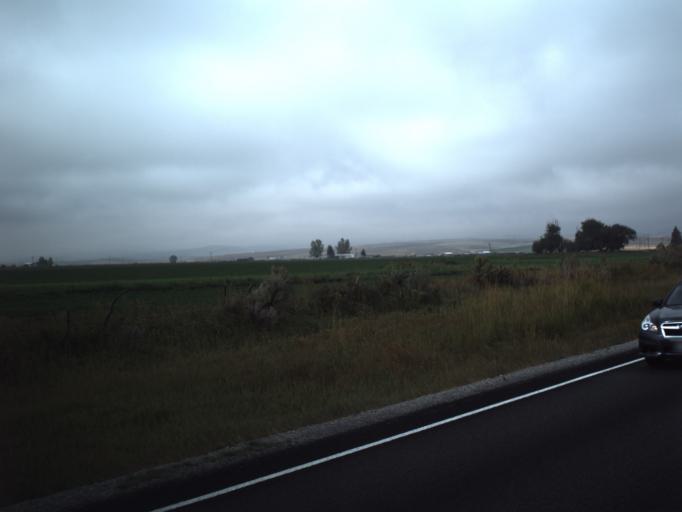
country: US
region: Utah
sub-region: Rich County
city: Randolph
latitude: 41.5174
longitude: -111.1445
